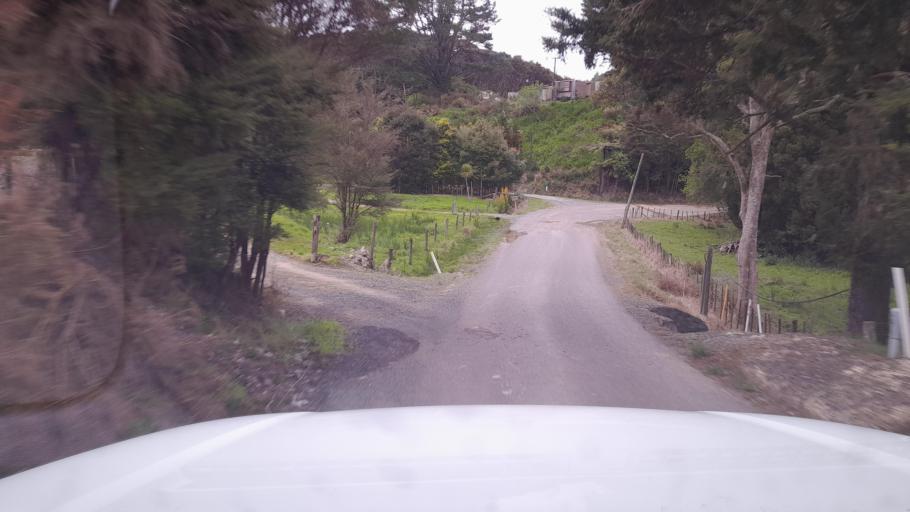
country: NZ
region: Northland
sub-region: Far North District
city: Paihia
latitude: -35.3409
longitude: 174.2339
